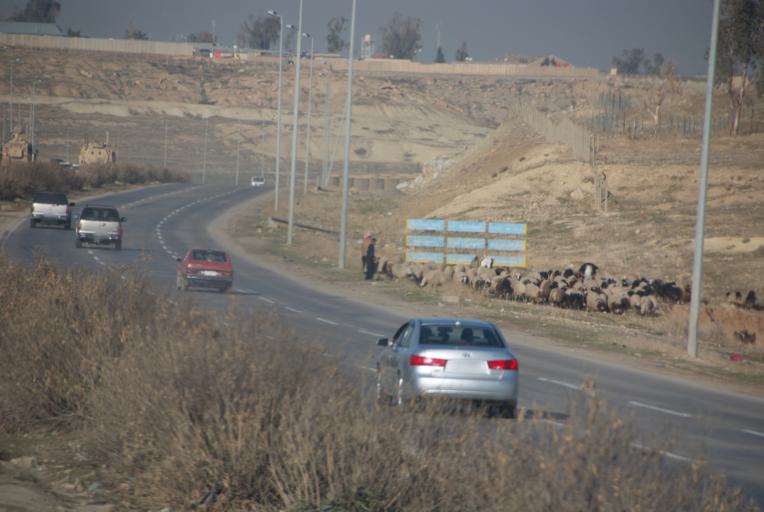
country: IQ
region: Ninawa
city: Al Mawsil al Jadidah
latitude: 36.2874
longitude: 43.1152
